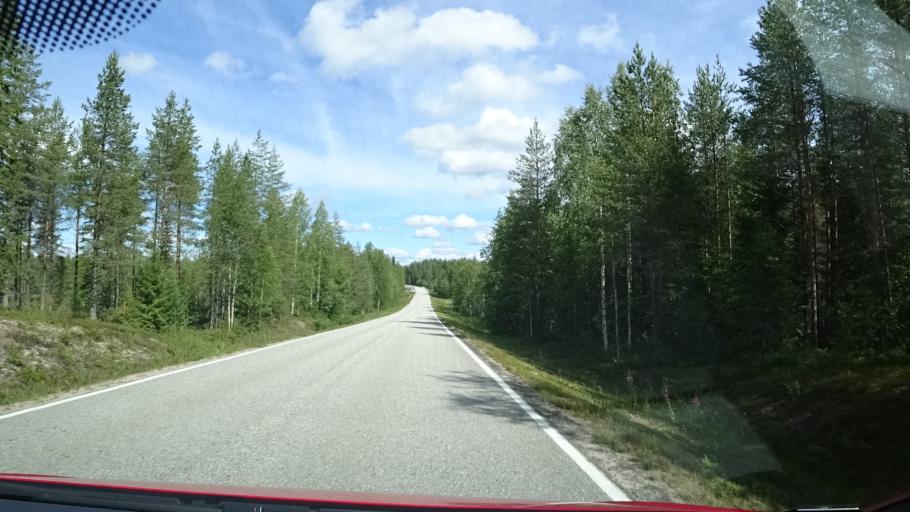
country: FI
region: Kainuu
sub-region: Kehys-Kainuu
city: Kuhmo
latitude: 64.5659
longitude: 29.6997
